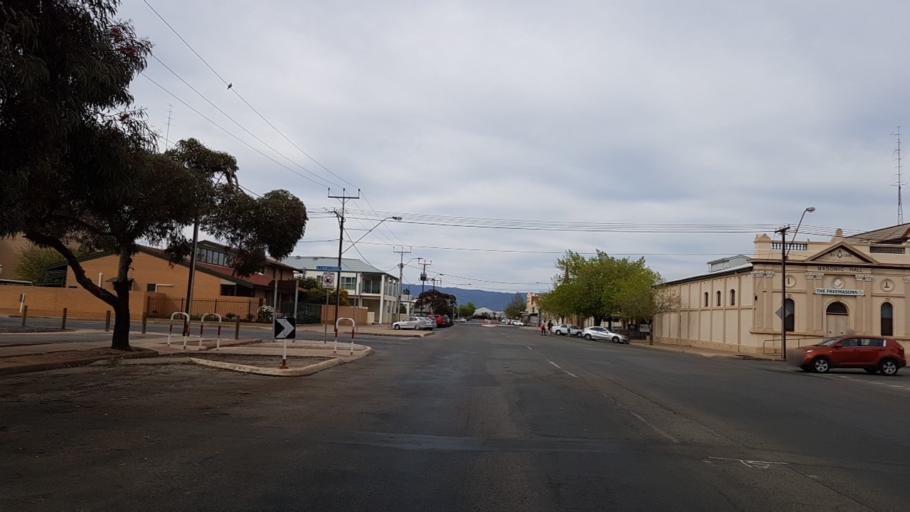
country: AU
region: South Australia
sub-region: Port Pirie City and Dists
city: Port Pirie
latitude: -33.1799
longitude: 138.0075
